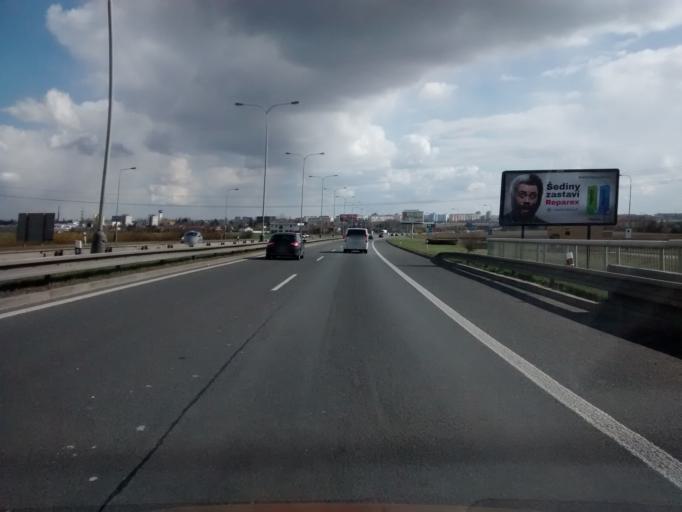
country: CZ
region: Praha
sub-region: Praha 9
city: Strizkov
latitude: 50.1569
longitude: 14.4855
